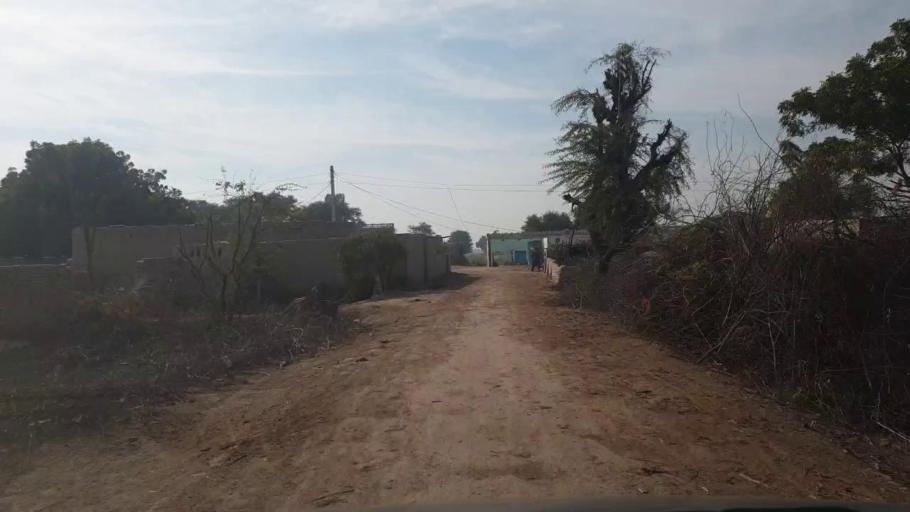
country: PK
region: Sindh
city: Shahpur Chakar
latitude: 26.1822
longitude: 68.5927
